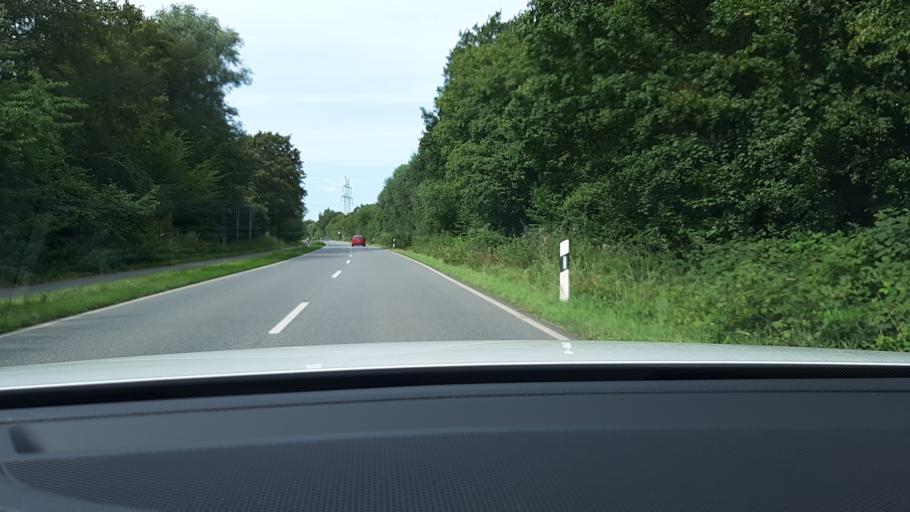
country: DE
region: Schleswig-Holstein
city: Monkhagen
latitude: 53.9059
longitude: 10.5476
